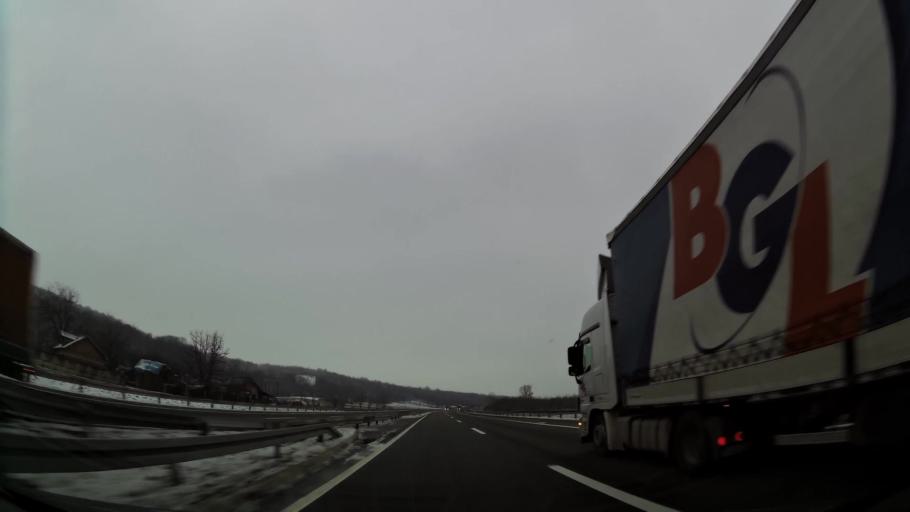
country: RS
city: Lugavcina
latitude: 44.4313
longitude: 21.0539
